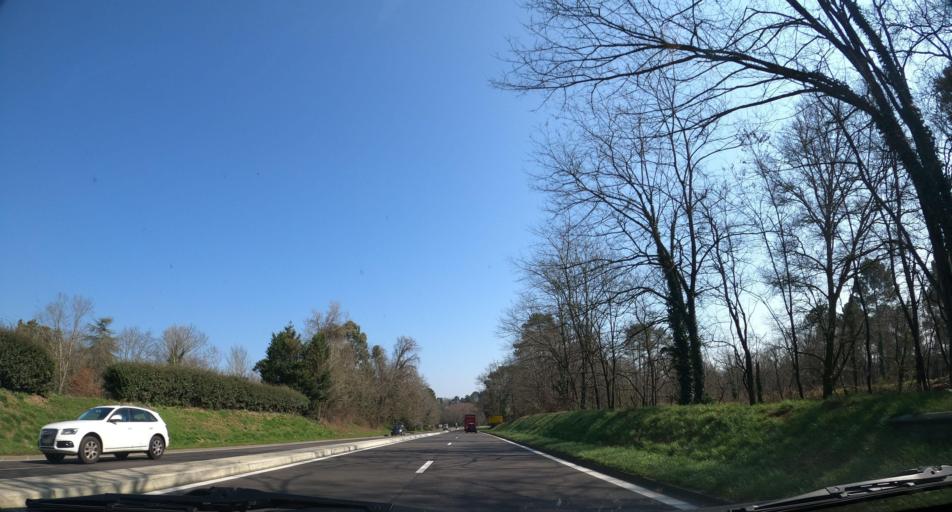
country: FR
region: Aquitaine
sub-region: Departement des Landes
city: Saint-Pierre-du-Mont
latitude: 43.8821
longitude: -0.5336
